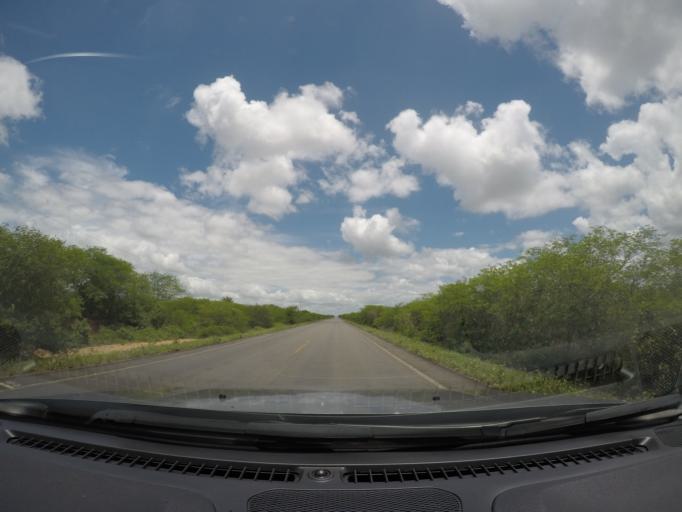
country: BR
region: Bahia
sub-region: Ipira
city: Ipira
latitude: -12.3516
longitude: -40.0125
